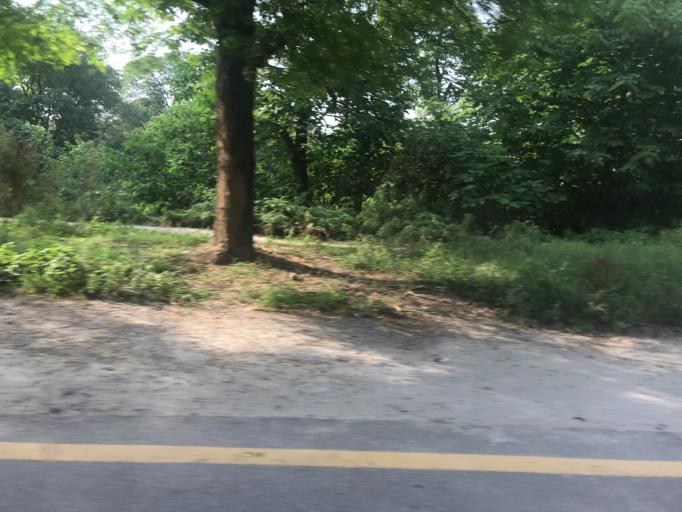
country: PK
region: Islamabad
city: Islamabad
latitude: 33.6958
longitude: 73.0481
